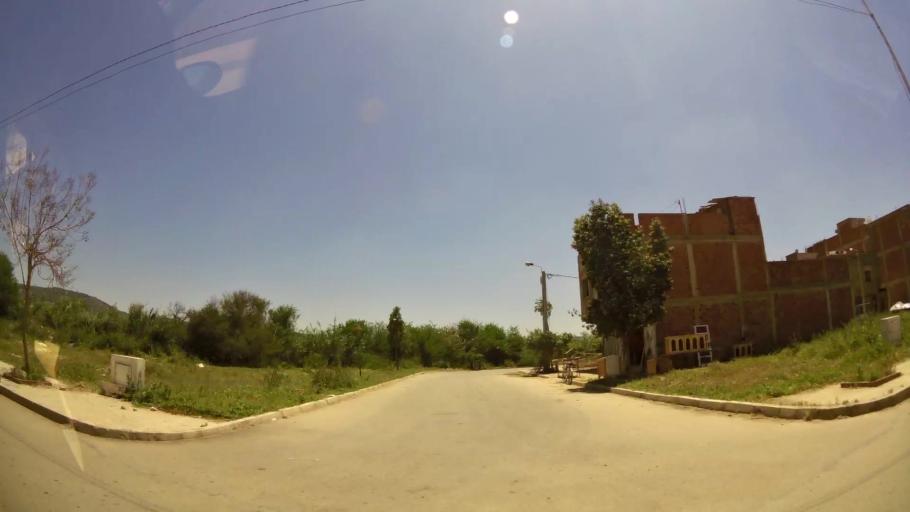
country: MA
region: Oriental
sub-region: Berkane-Taourirt
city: Madagh
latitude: 35.0746
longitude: -2.2243
